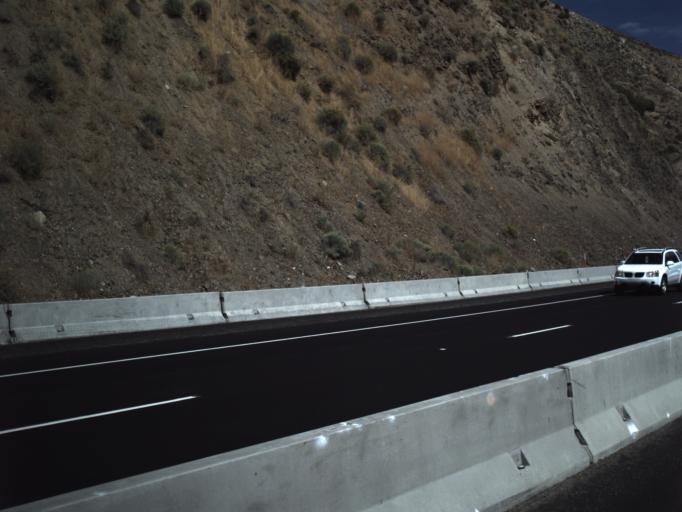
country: US
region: Utah
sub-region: Box Elder County
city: Brigham City
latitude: 41.4979
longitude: -111.9767
